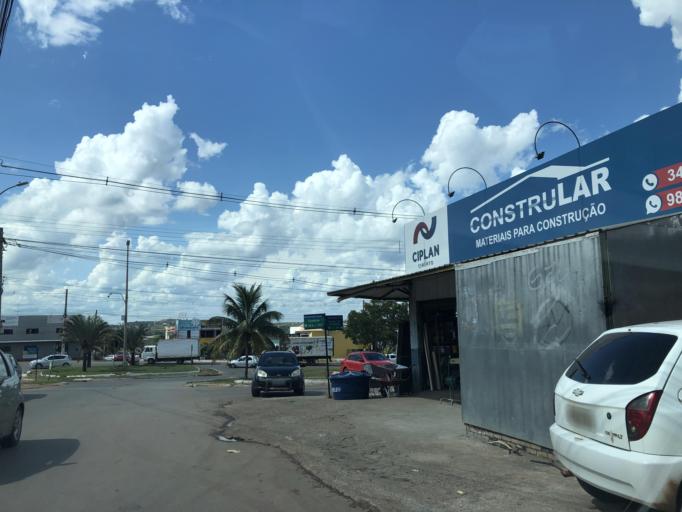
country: BR
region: Federal District
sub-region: Brasilia
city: Brasilia
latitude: -15.8991
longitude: -47.7823
